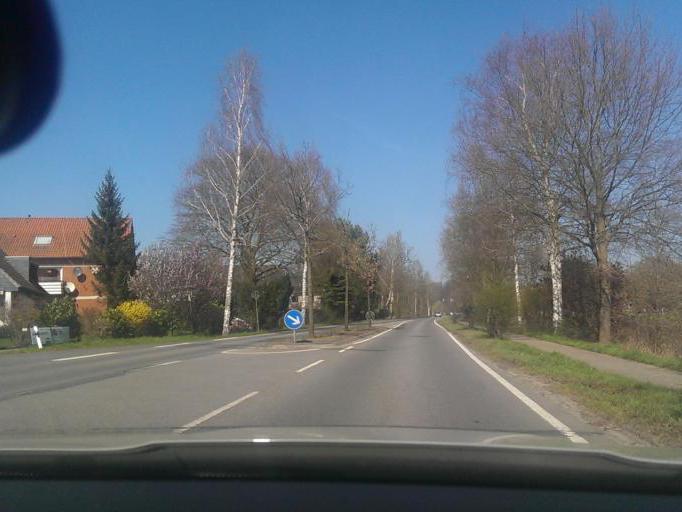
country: DE
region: Lower Saxony
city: Garbsen-Mitte
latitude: 52.5032
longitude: 9.6302
